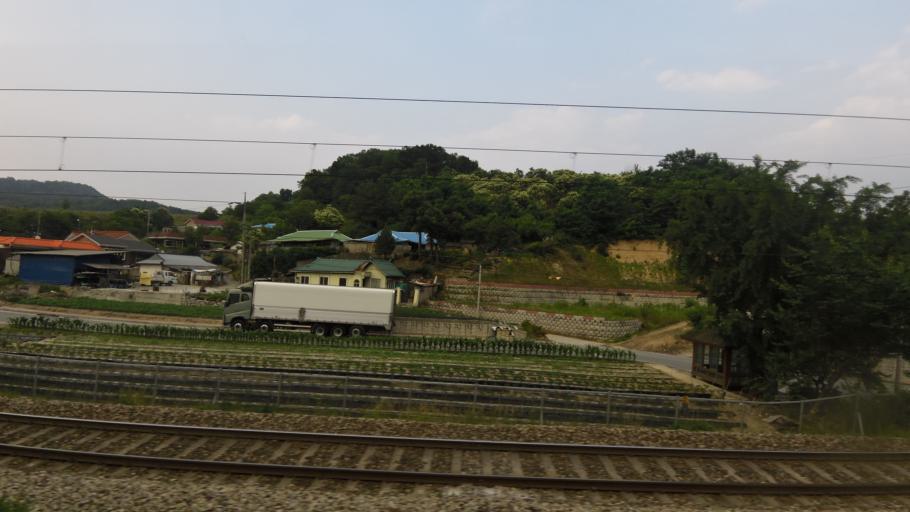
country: KR
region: Daejeon
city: Sintansin
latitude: 36.5280
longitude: 127.3733
